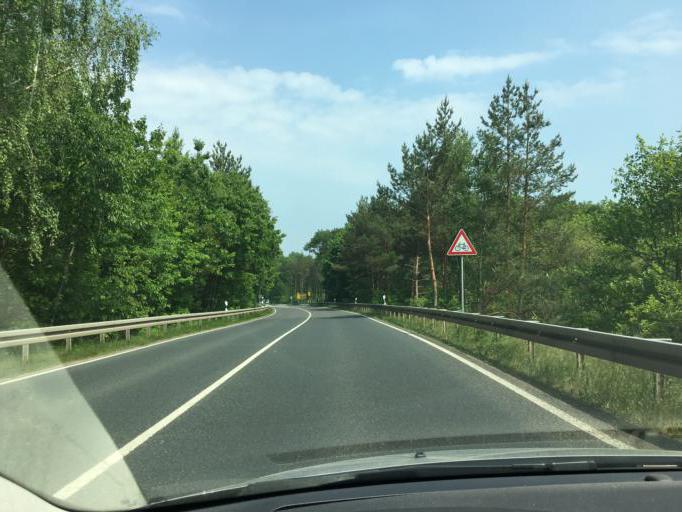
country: DE
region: Saxony
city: Naunhof
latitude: 51.2900
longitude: 12.5884
